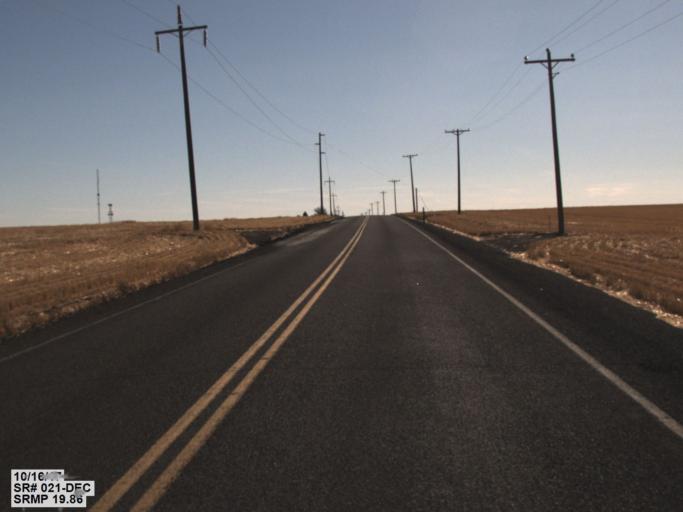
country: US
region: Washington
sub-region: Adams County
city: Ritzville
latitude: 46.9078
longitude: -118.5678
